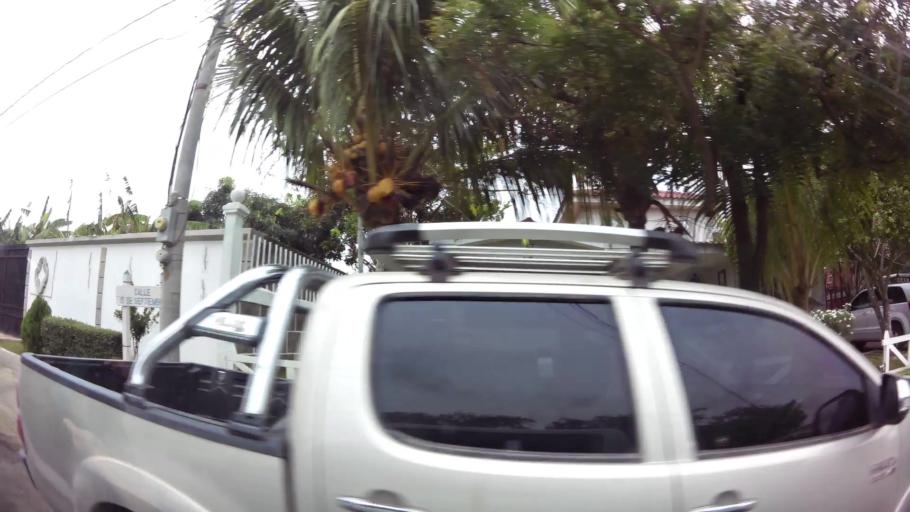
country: NI
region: Masaya
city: Ticuantepe
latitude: 12.0605
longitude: -86.1969
